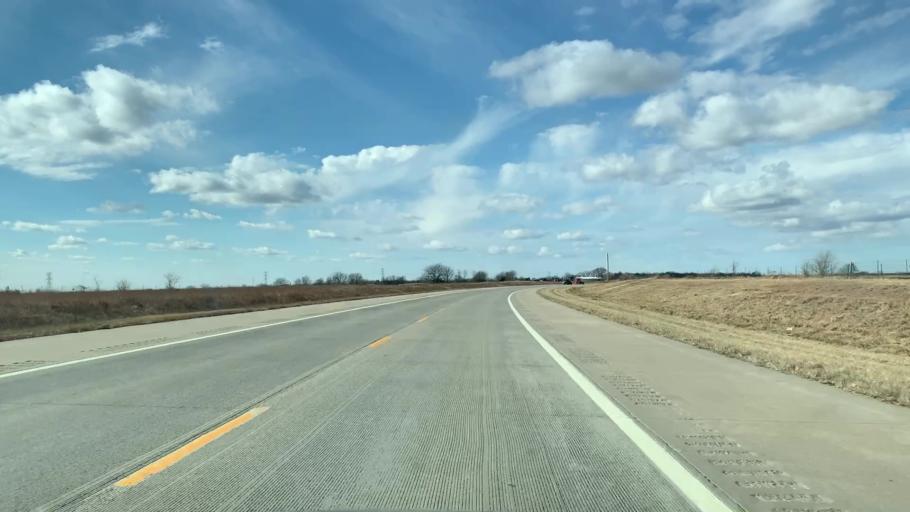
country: US
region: Kansas
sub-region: Labette County
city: Parsons
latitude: 37.3510
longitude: -95.2029
